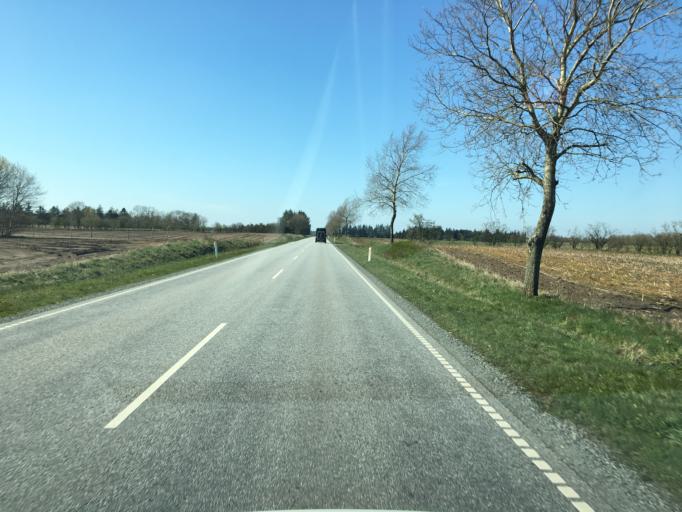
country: DK
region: South Denmark
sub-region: Aabenraa Kommune
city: Tinglev
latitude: 54.9451
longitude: 9.3549
